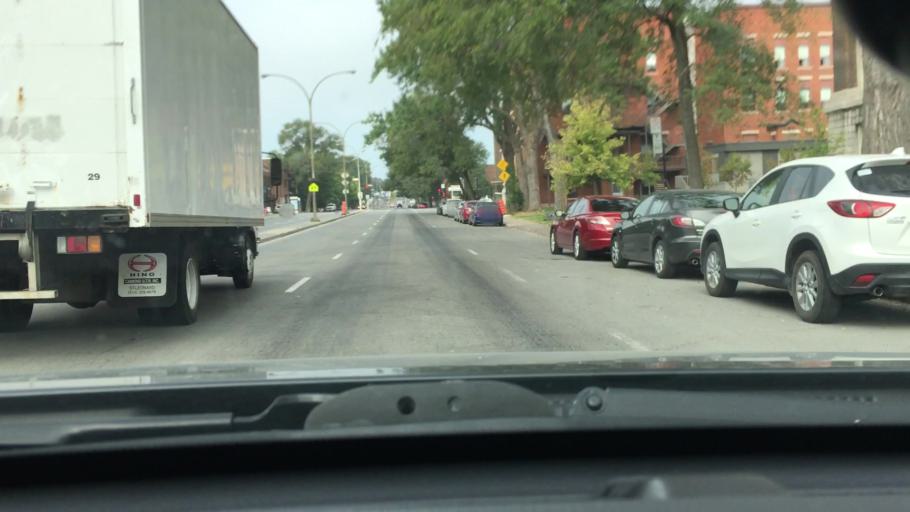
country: CA
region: Quebec
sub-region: Monteregie
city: Longueuil
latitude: 45.5521
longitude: -73.5465
